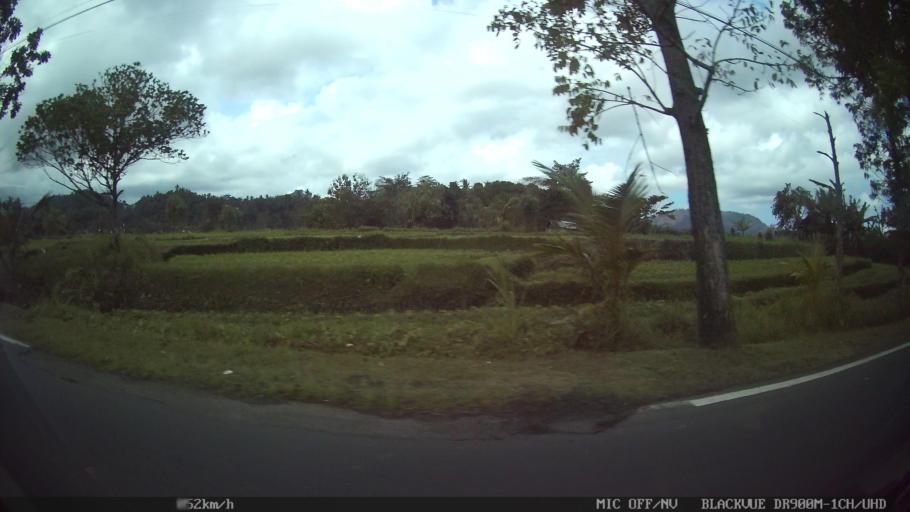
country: ID
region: Bali
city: Banjar Wangsian
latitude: -8.4876
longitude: 115.4014
